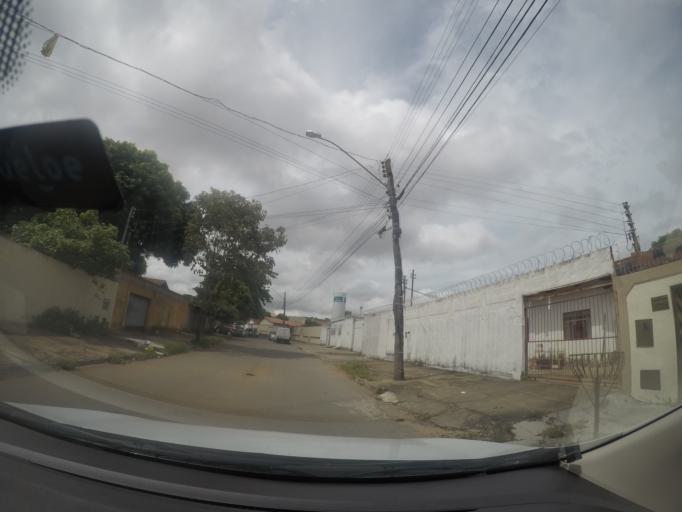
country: BR
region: Goias
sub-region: Goiania
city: Goiania
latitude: -16.7146
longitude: -49.3061
